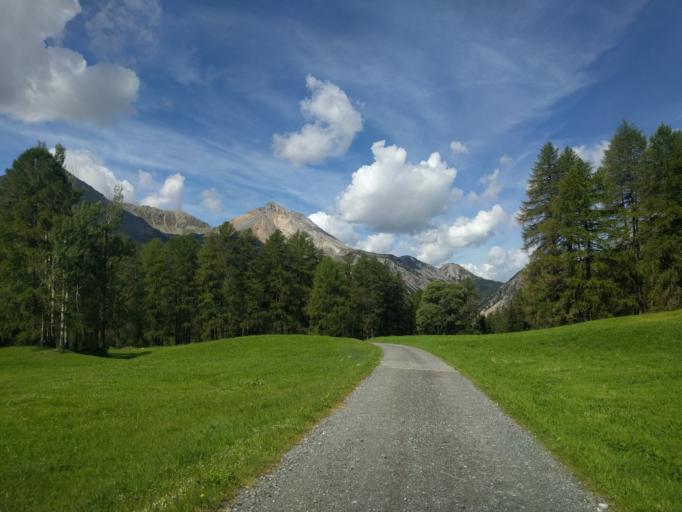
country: IT
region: Trentino-Alto Adige
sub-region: Bolzano
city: Tubre
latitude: 46.6256
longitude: 10.3593
